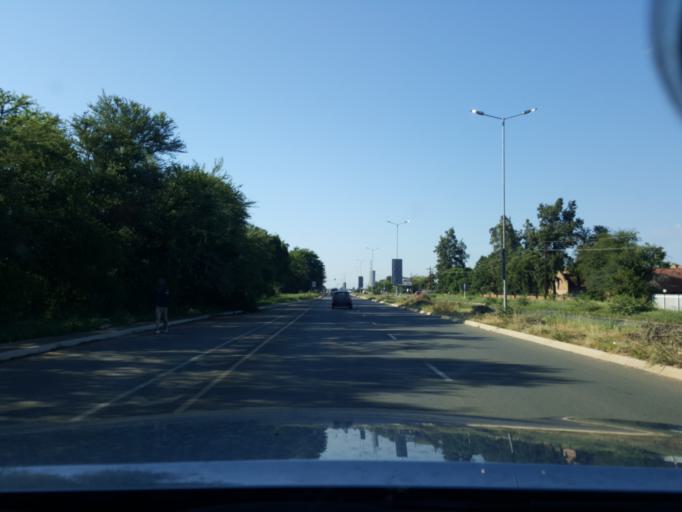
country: ZA
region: North-West
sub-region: Ngaka Modiri Molema District Municipality
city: Mmabatho
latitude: -25.8145
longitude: 25.6338
